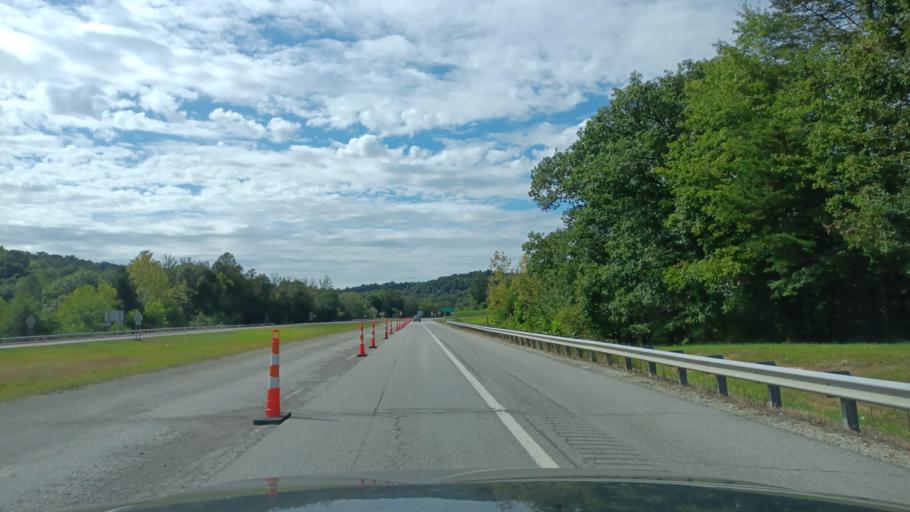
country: US
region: West Virginia
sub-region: Ritchie County
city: Harrisville
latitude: 39.2606
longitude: -81.0700
